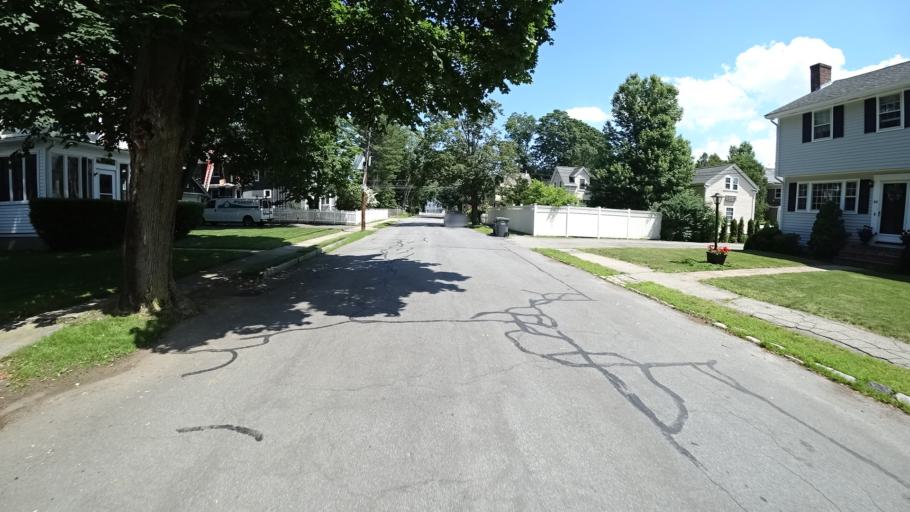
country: US
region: Massachusetts
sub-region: Norfolk County
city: Dedham
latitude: 42.2439
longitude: -71.1792
